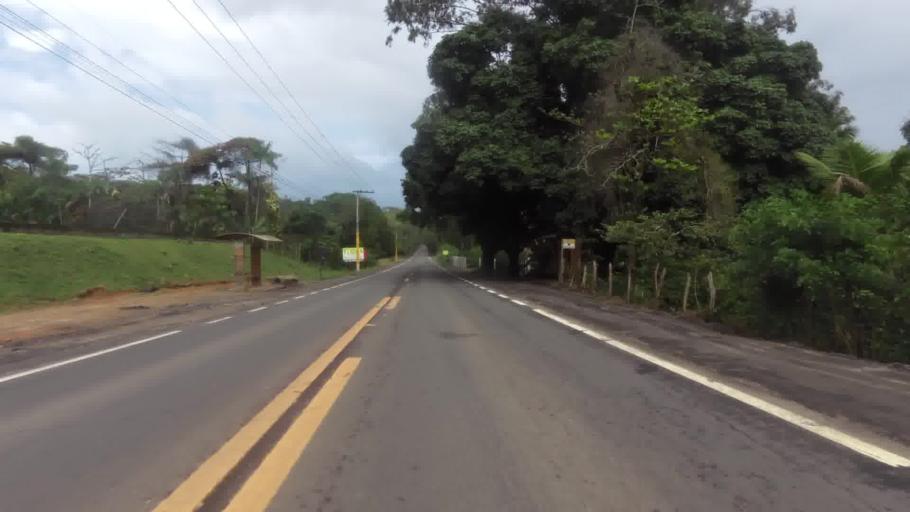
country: BR
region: Espirito Santo
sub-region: Piuma
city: Piuma
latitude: -20.8177
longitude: -40.6908
